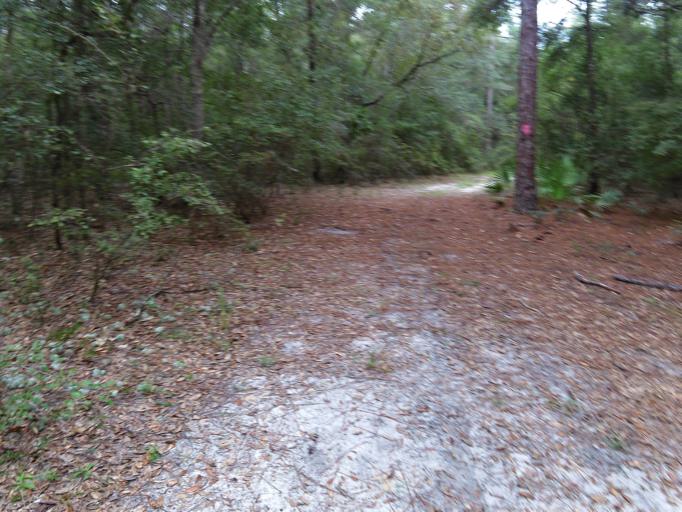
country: US
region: Florida
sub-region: Clay County
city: Middleburg
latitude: 30.1406
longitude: -81.9501
